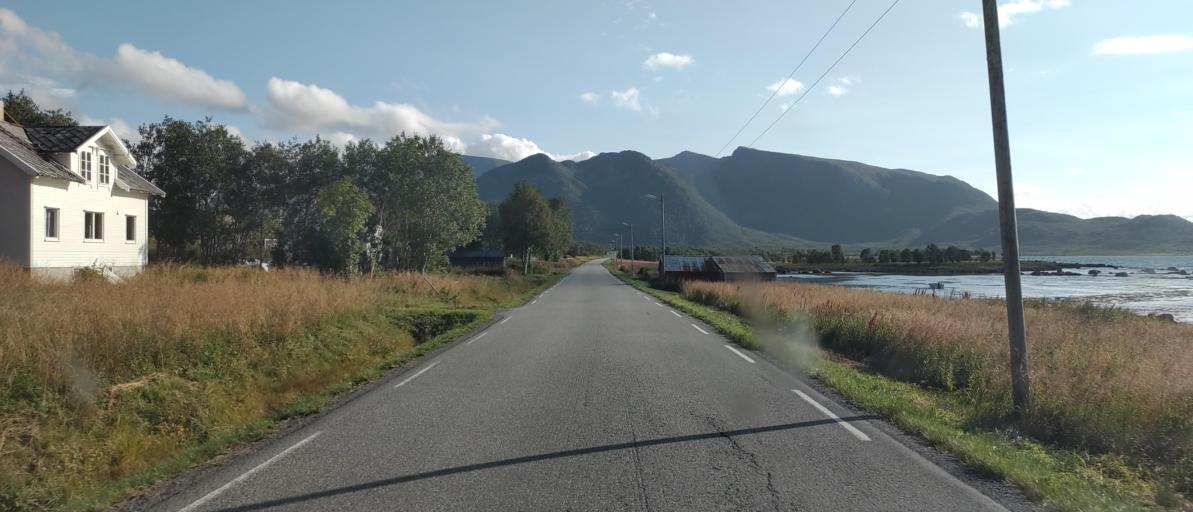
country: NO
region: Nordland
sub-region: Sortland
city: Sortland
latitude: 68.9053
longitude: 15.6125
